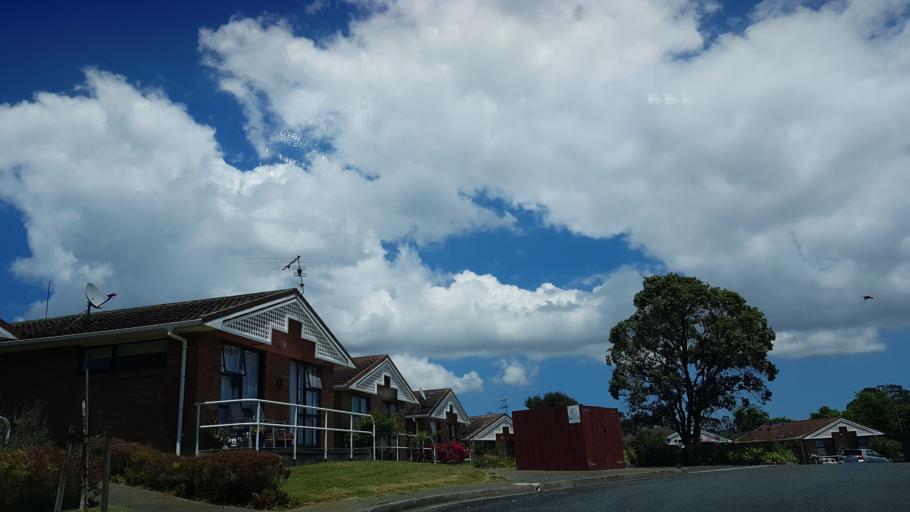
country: NZ
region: Auckland
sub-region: Auckland
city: North Shore
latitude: -36.7901
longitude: 174.6899
